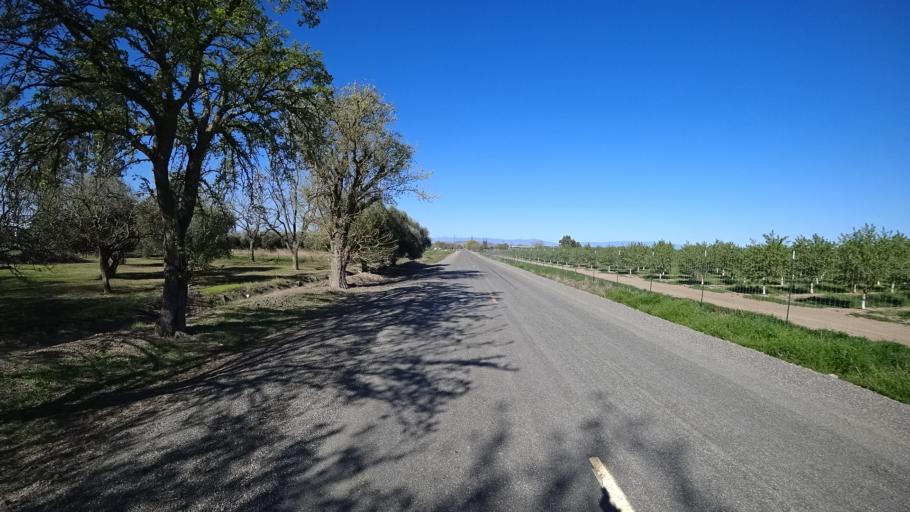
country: US
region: California
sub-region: Glenn County
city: Orland
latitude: 39.7476
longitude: -122.2228
